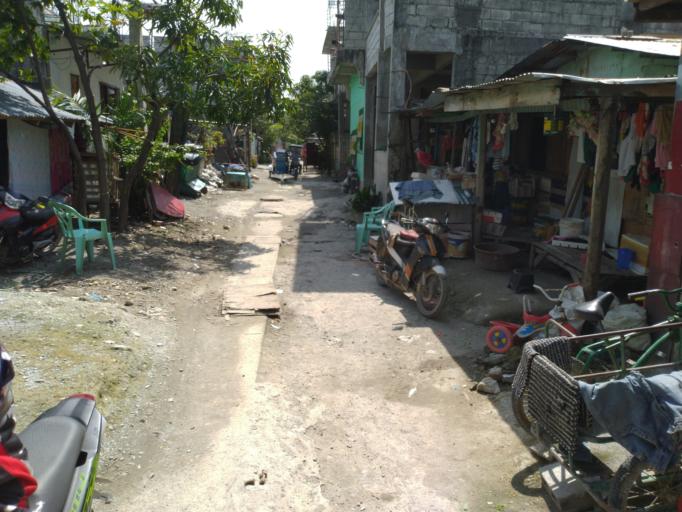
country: PH
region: Calabarzon
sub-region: Province of Rizal
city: Taytay
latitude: 14.5391
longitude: 121.1112
